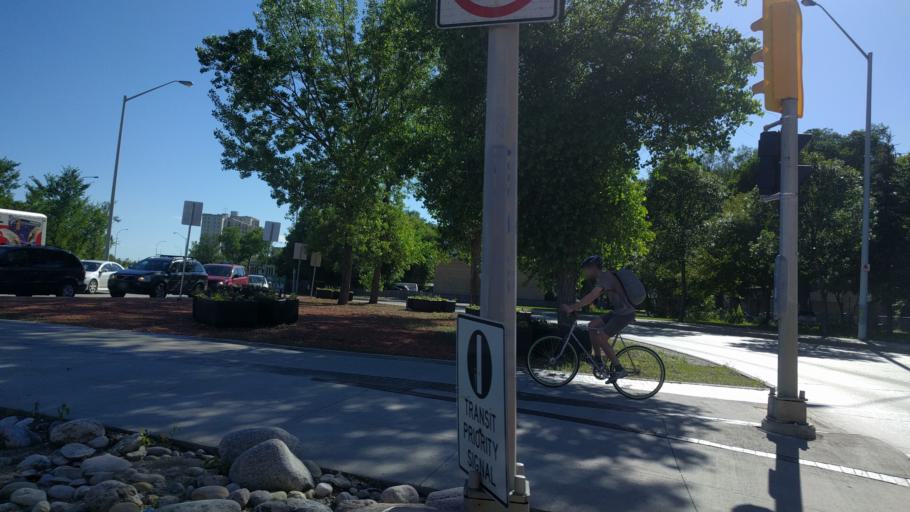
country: CA
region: Manitoba
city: Winnipeg
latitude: 49.8838
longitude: -97.1319
